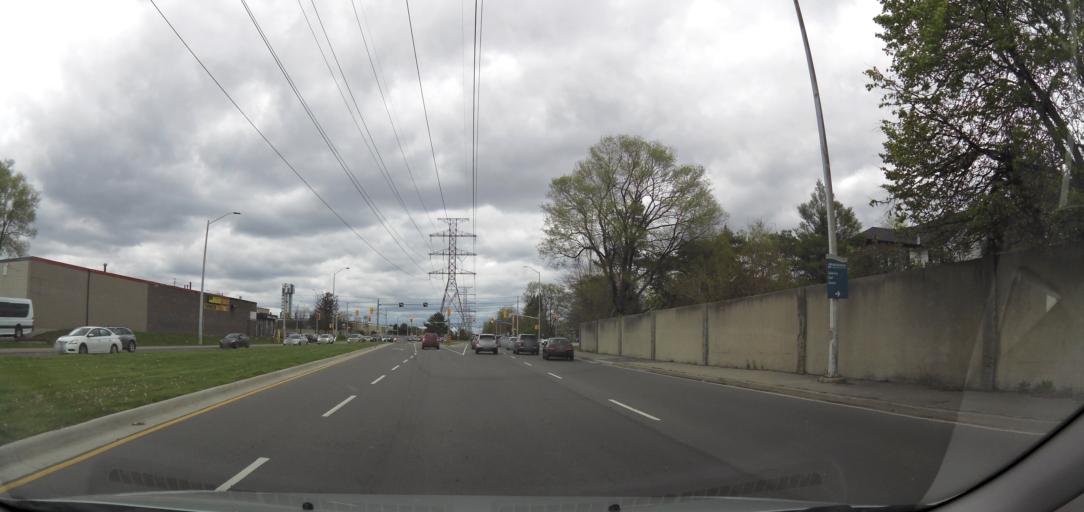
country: CA
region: Ontario
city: Etobicoke
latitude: 43.6021
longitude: -79.5756
